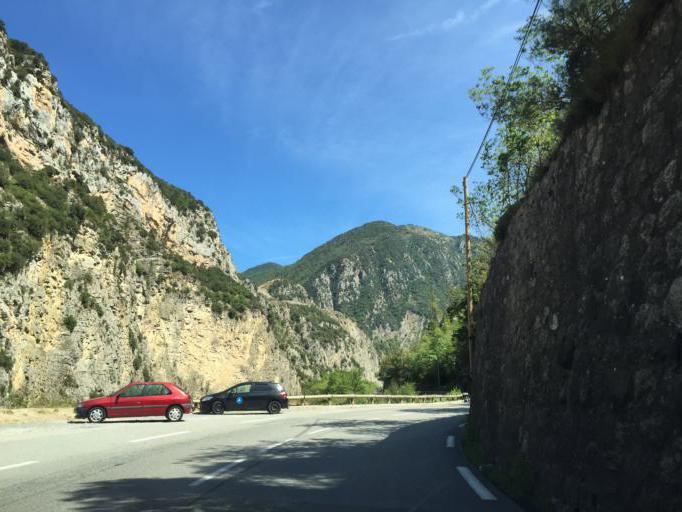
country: FR
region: Provence-Alpes-Cote d'Azur
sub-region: Departement des Alpes-Maritimes
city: Gilette
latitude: 43.9320
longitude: 7.1753
